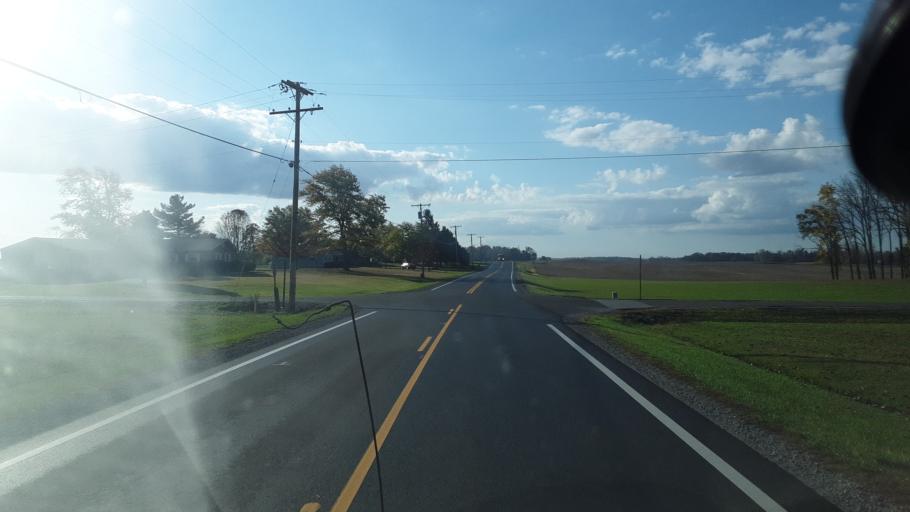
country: US
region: Ohio
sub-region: Fayette County
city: Jeffersonville
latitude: 39.6145
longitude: -83.5266
